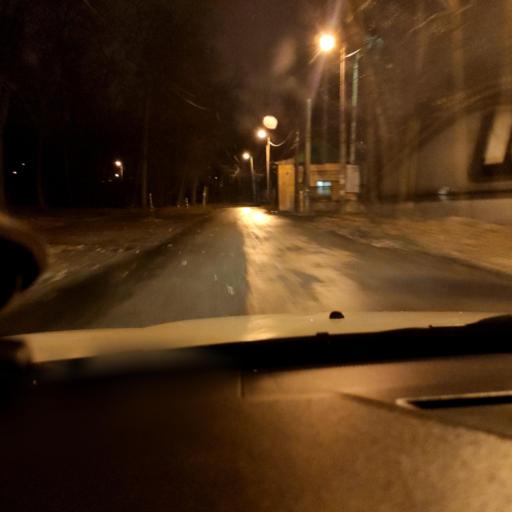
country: RU
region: Samara
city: Samara
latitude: 53.2898
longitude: 50.1975
